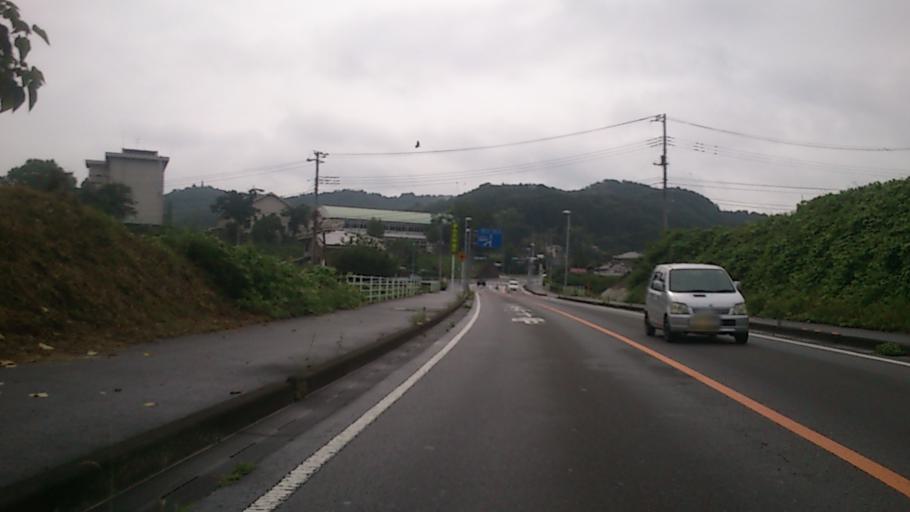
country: JP
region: Tochigi
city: Karasuyama
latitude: 36.7332
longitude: 140.1721
